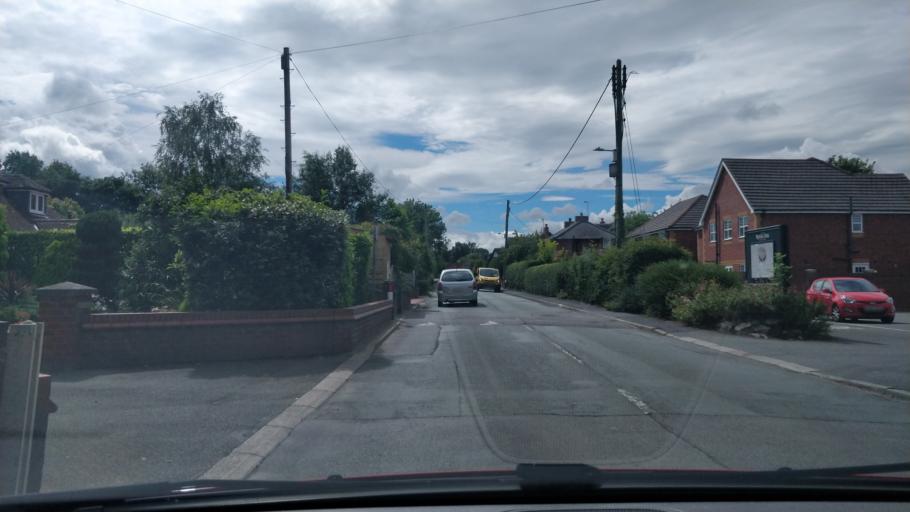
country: GB
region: Wales
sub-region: County of Flintshire
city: Hope
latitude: 53.1473
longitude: -3.0002
